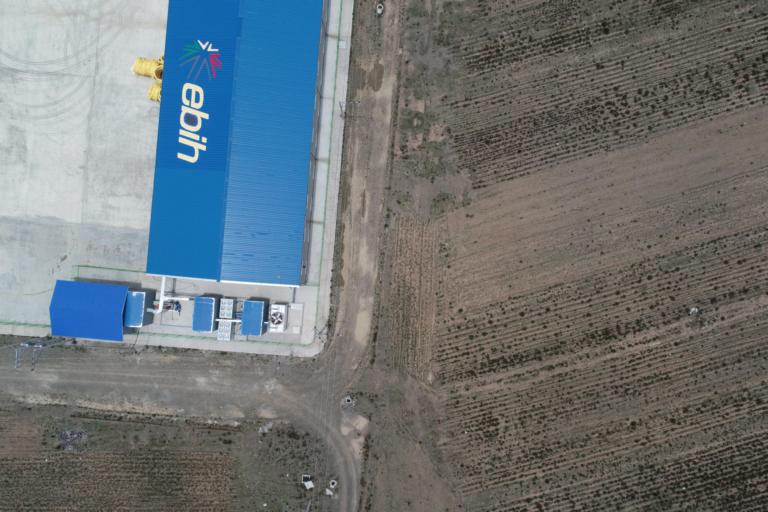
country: BO
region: La Paz
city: La Paz
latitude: -16.5187
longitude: -68.2968
